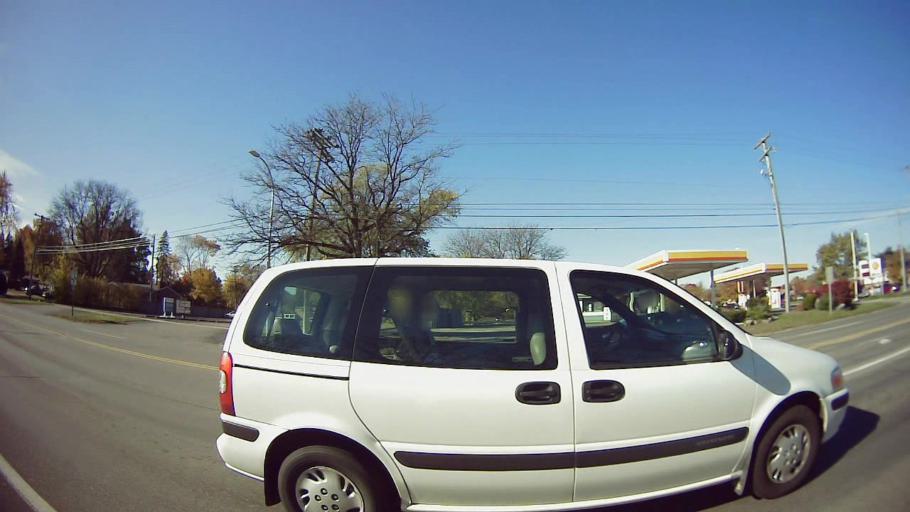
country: US
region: Michigan
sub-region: Wayne County
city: Livonia
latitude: 42.4111
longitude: -83.3741
